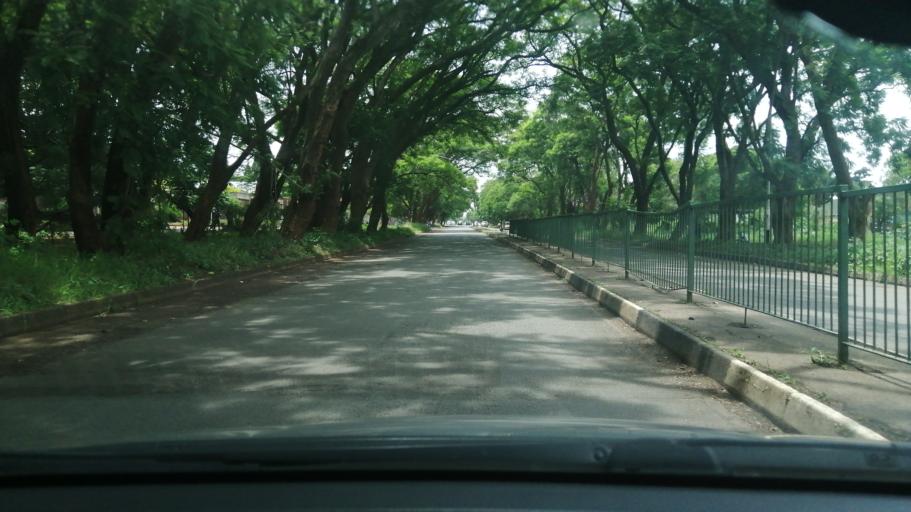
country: ZW
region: Harare
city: Harare
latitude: -17.8145
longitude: 31.0416
